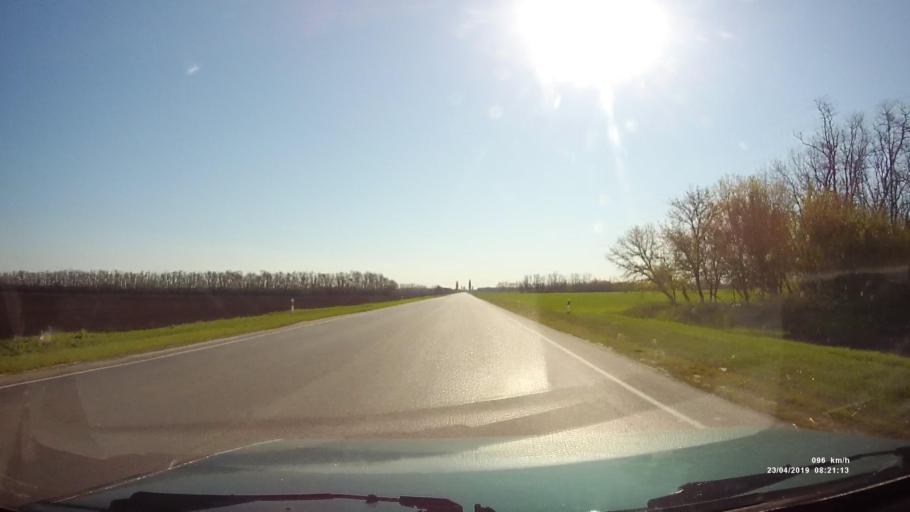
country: RU
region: Rostov
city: Tselina
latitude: 46.5356
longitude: 40.8859
